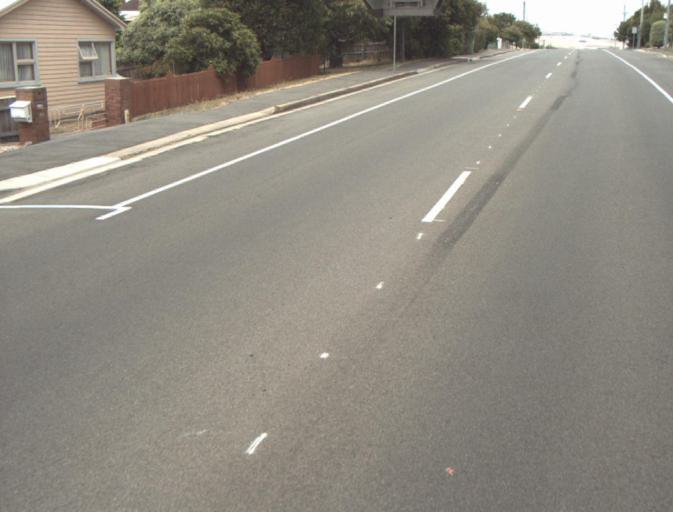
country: AU
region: Tasmania
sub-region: Launceston
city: Newstead
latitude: -41.4574
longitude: 147.1794
